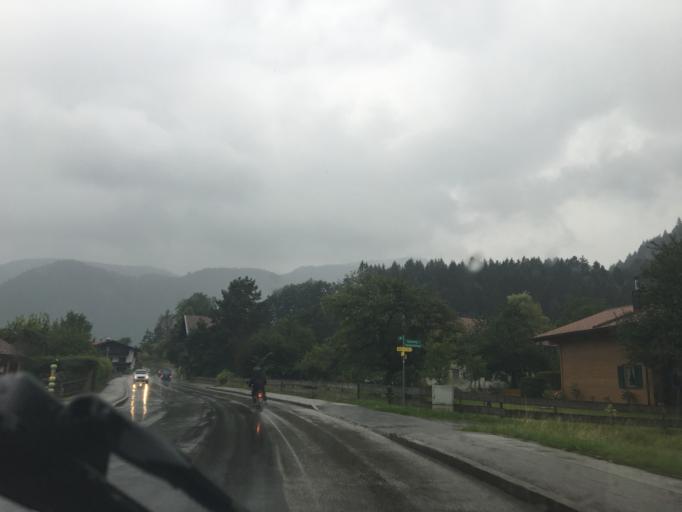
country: DE
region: Bavaria
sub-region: Upper Bavaria
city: Unterwossen
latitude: 47.7171
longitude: 12.4765
